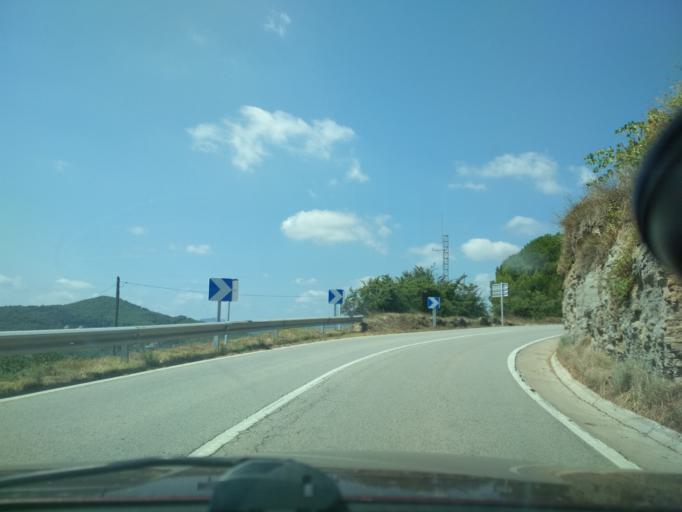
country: ES
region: Catalonia
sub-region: Provincia de Barcelona
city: Sant Feliu de Codines
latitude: 41.6942
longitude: 2.1703
